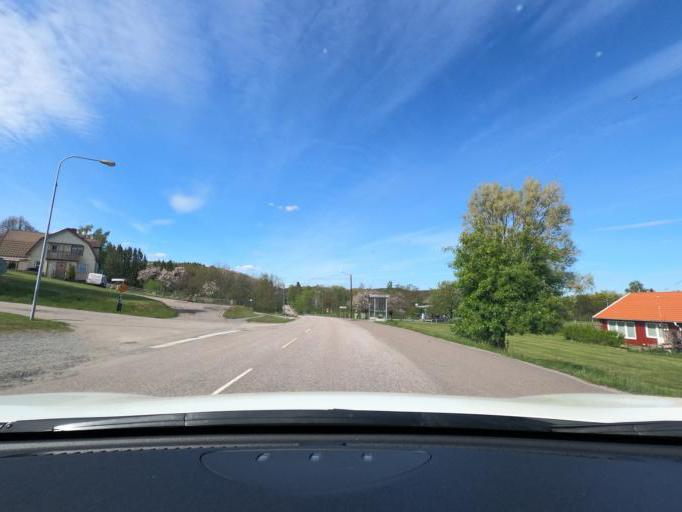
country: SE
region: Vaestra Goetaland
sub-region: Marks Kommun
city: Kinna
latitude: 57.4676
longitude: 12.5937
